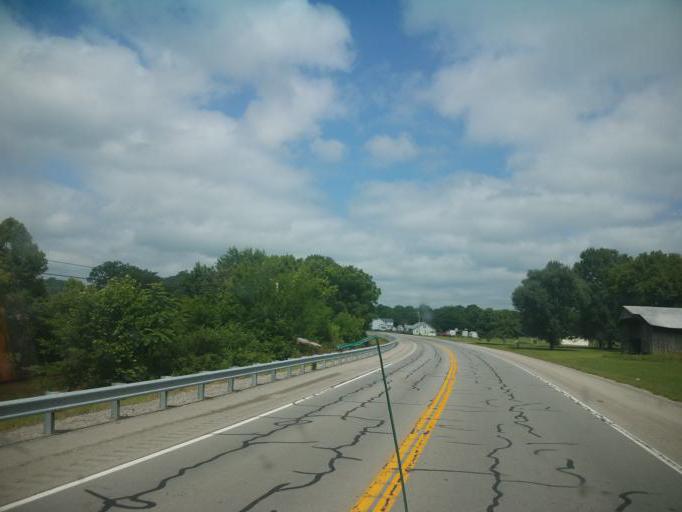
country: US
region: Kentucky
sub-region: Cumberland County
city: Burkesville
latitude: 36.8378
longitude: -85.5200
